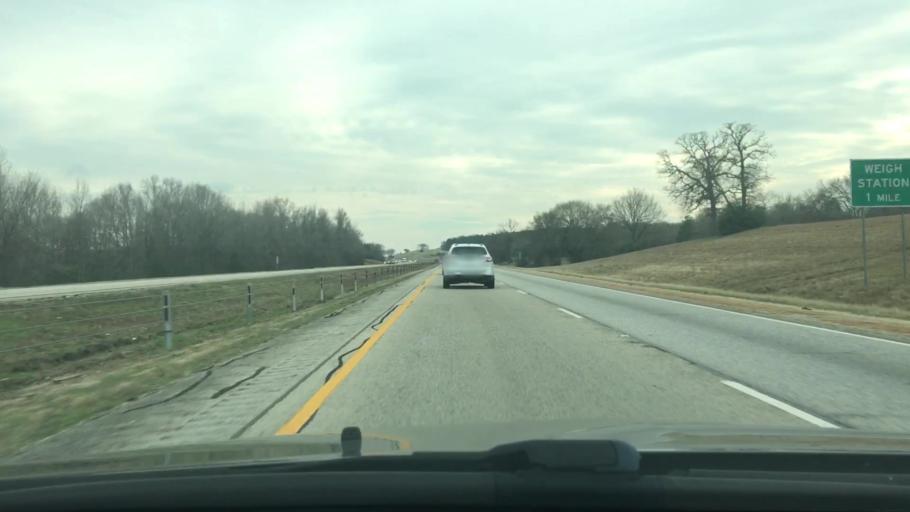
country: US
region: Texas
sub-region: Leon County
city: Centerville
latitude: 31.2995
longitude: -95.9996
